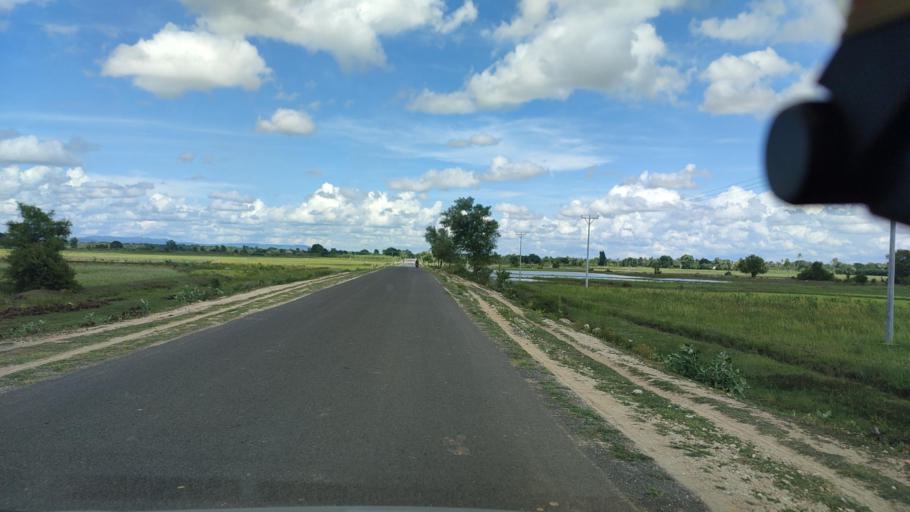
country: MM
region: Magway
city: Taungdwingyi
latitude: 20.1934
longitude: 95.4155
